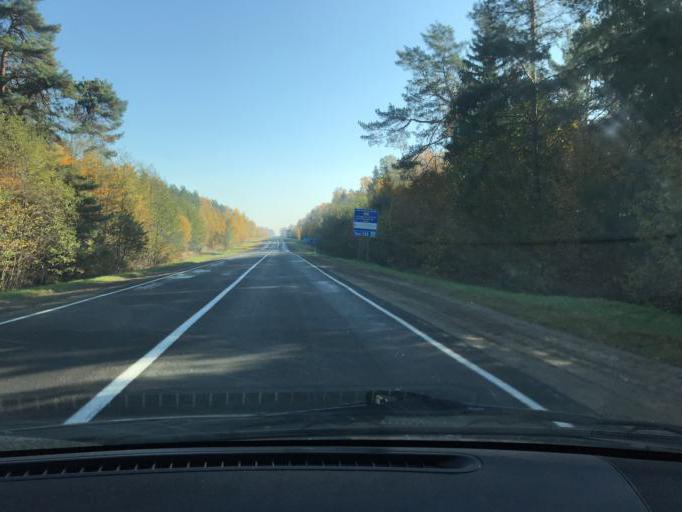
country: BY
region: Brest
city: Lyakhavichy
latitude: 52.9601
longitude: 26.3983
